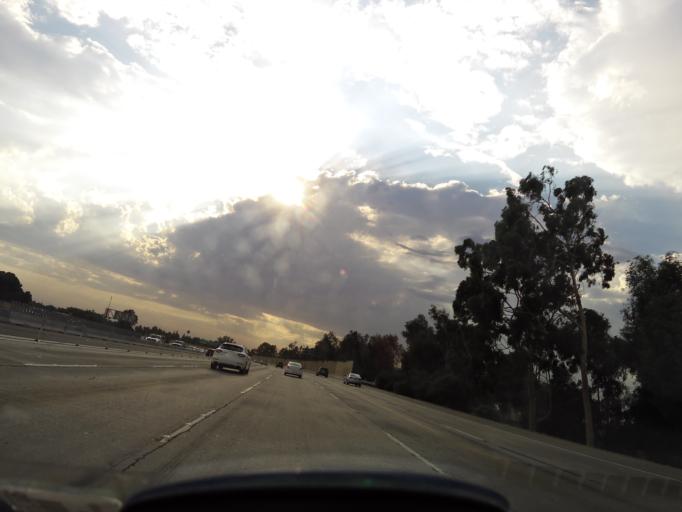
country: US
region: California
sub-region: Orange County
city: Yorba Linda
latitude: 33.8544
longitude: -117.8047
